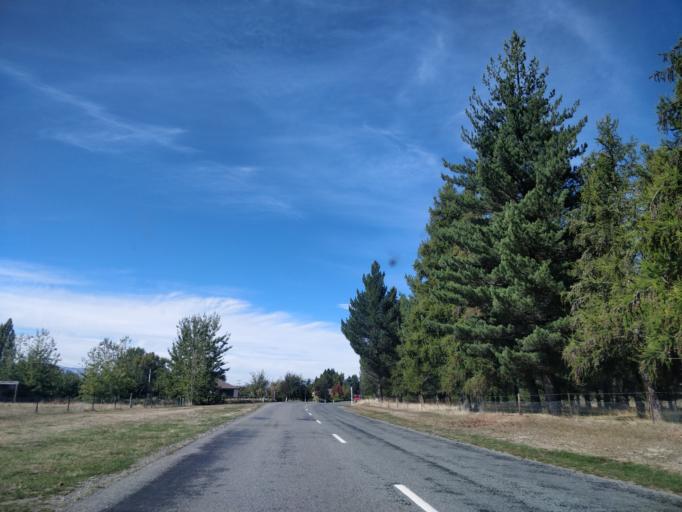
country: NZ
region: Canterbury
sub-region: Timaru District
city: Pleasant Point
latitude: -44.2453
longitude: 170.0928
